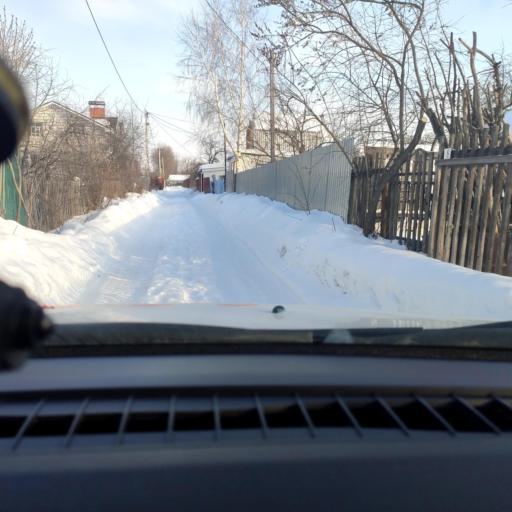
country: RU
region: Samara
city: Samara
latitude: 53.1297
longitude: 50.2524
